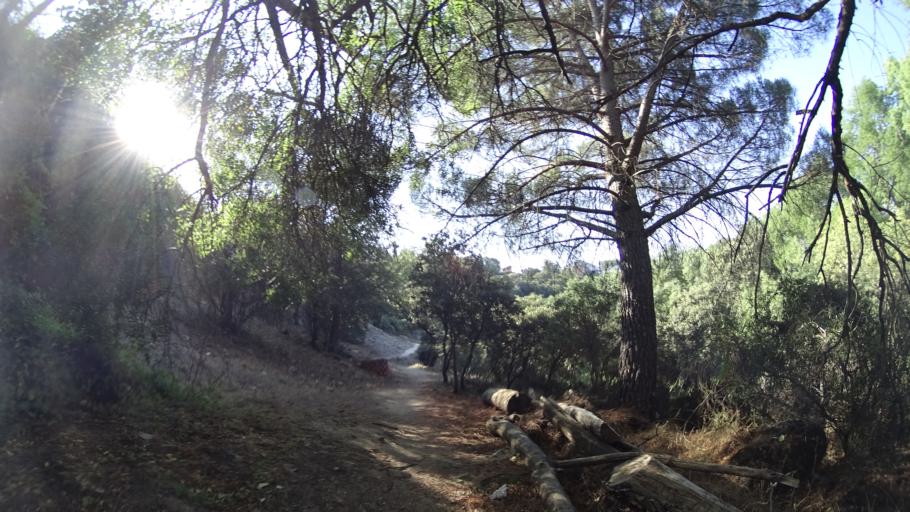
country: ES
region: Madrid
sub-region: Provincia de Madrid
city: Las Matas
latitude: 40.5812
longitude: -3.8954
